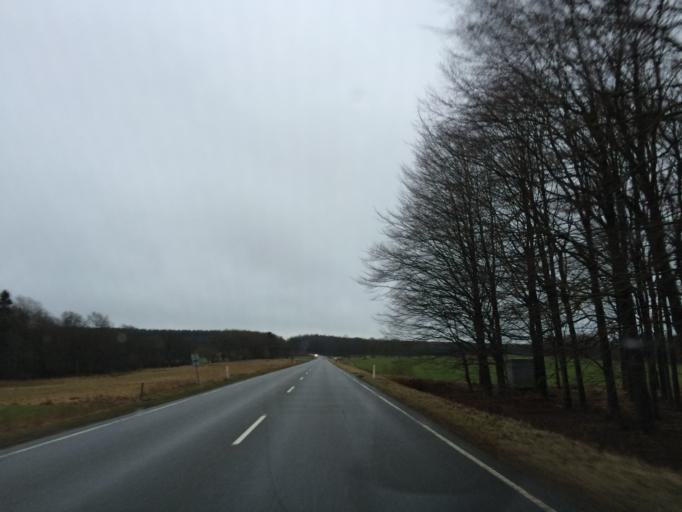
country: DK
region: North Denmark
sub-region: Mariagerfjord Kommune
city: Arden
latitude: 56.8103
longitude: 9.8185
